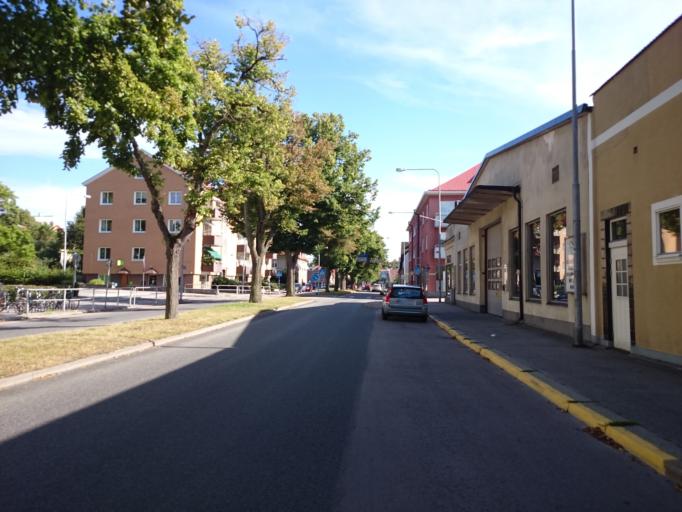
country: SE
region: Blekinge
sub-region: Karlshamns Kommun
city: Karlshamn
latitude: 56.1705
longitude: 14.8687
